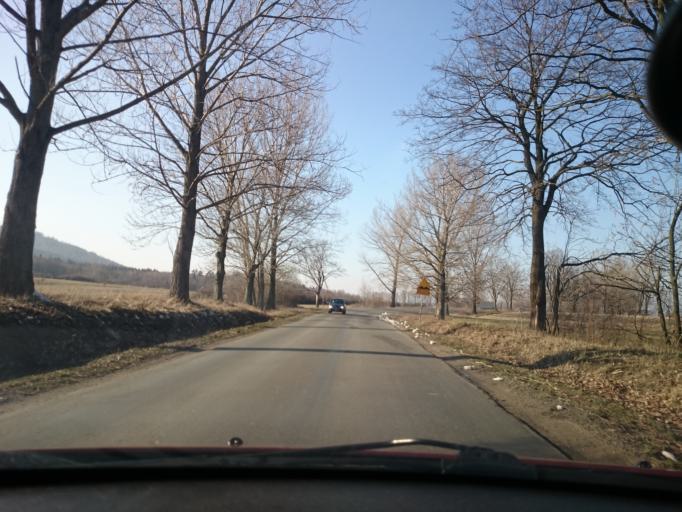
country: PL
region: Lower Silesian Voivodeship
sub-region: Powiat klodzki
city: Bystrzyca Klodzka
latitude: 50.3168
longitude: 16.6147
